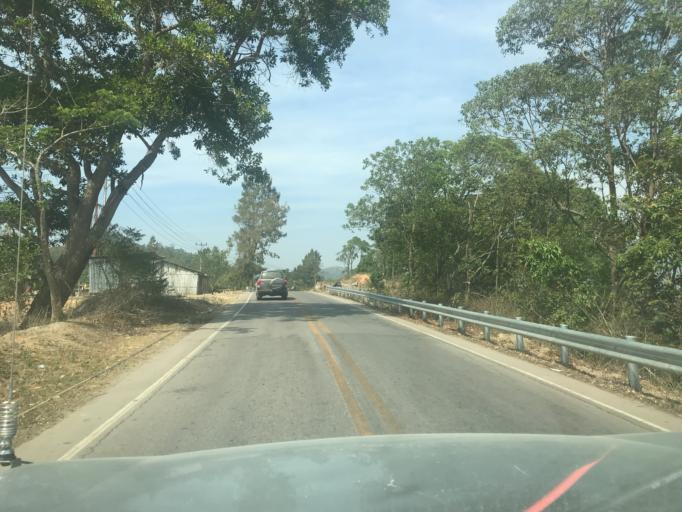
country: TL
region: Aileu
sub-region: Aileu Villa
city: Aileu
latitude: -8.6824
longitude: 125.5503
